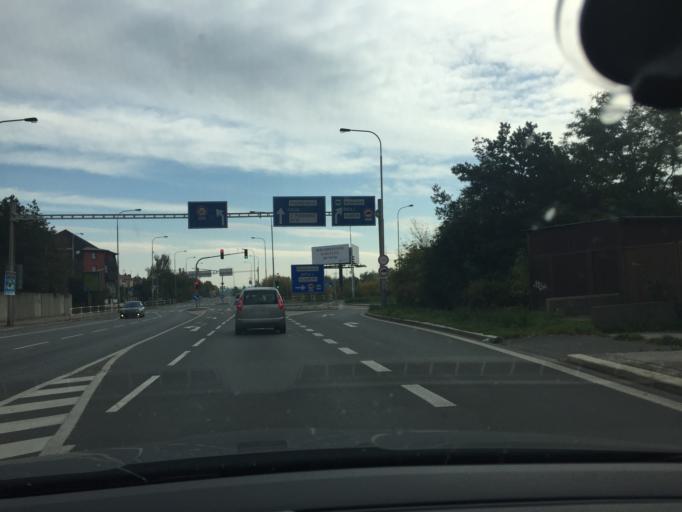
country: CZ
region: Praha
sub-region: Praha 9
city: Vysocany
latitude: 50.0922
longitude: 14.5334
